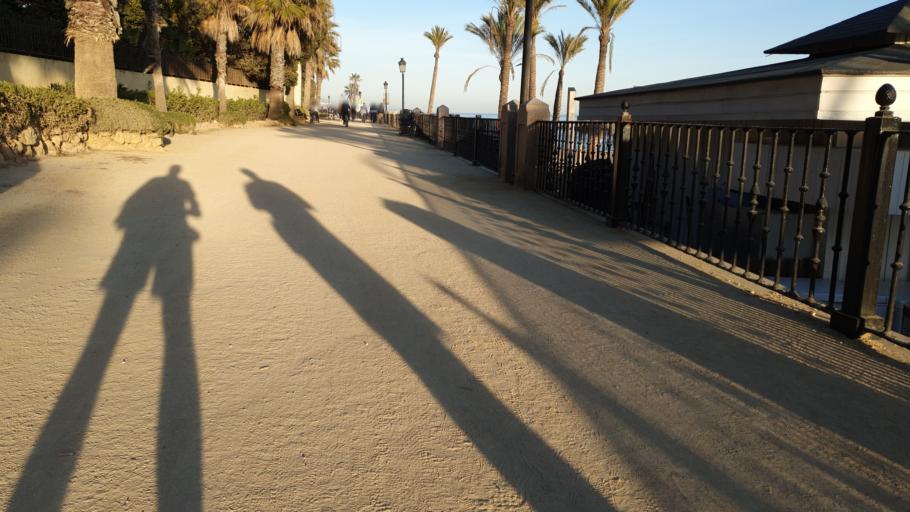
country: ES
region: Andalusia
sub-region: Provincia de Malaga
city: Marbella
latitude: 36.5061
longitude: -4.9103
